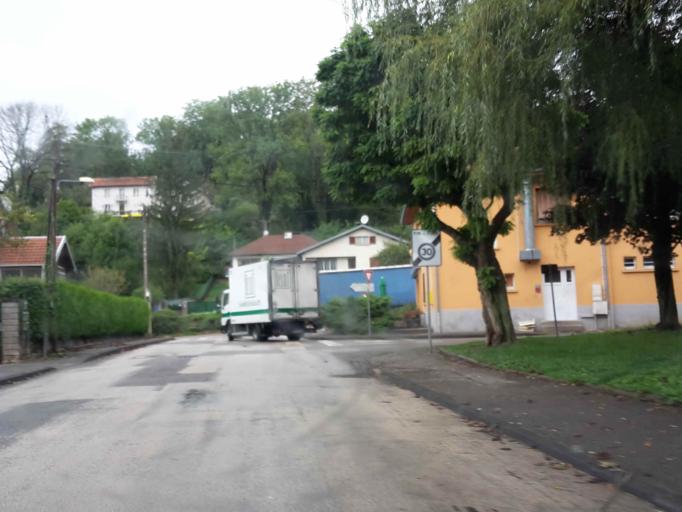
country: FR
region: Franche-Comte
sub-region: Departement du Doubs
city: Baume-les-Dames
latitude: 47.3504
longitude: 6.3680
